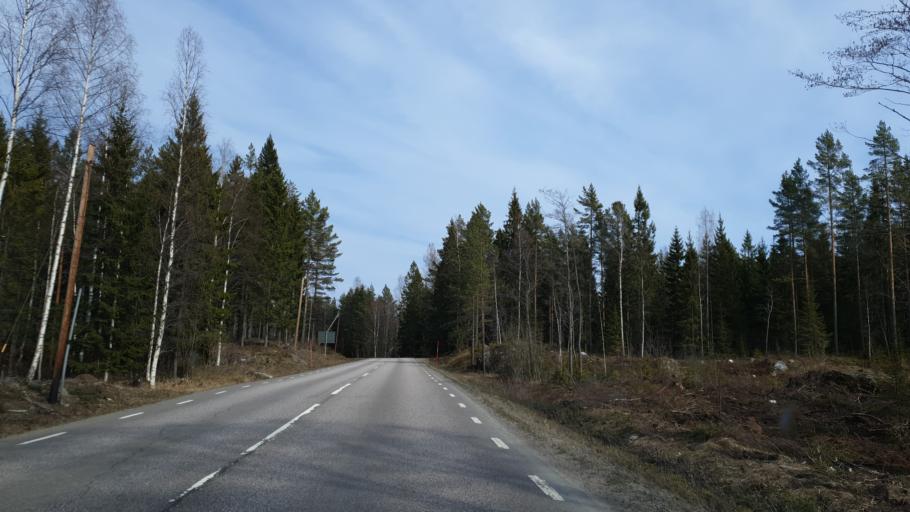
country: SE
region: Gaevleborg
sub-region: Gavle Kommun
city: Norrsundet
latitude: 60.9611
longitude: 17.0395
